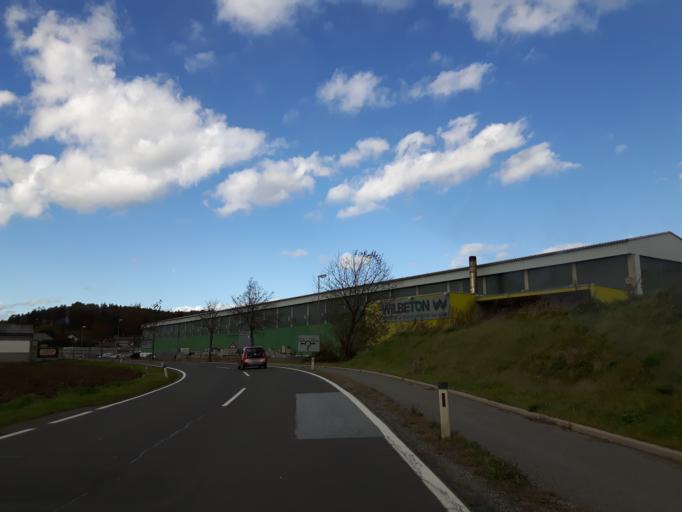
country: AT
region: Styria
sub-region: Politischer Bezirk Suedoststeiermark
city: Kirchbach in Steiermark
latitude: 46.9125
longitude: 15.6777
